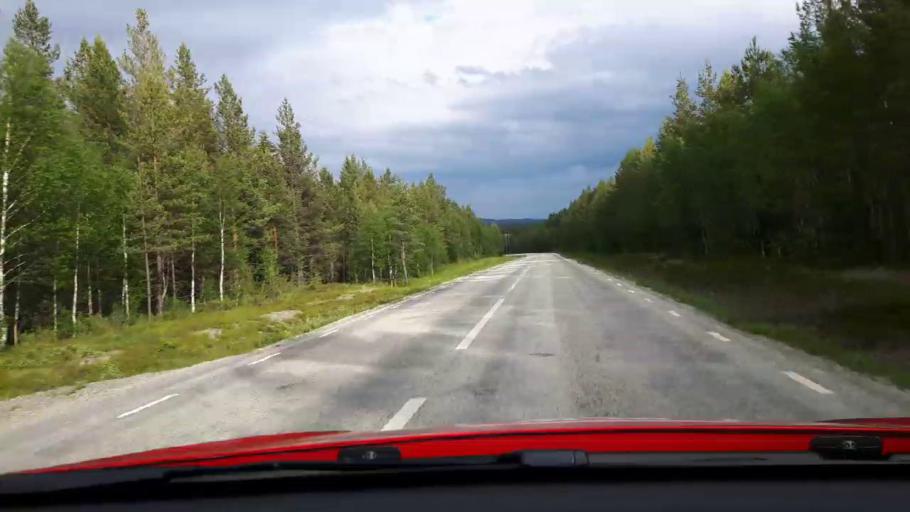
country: SE
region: Jaemtland
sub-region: Bergs Kommun
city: Hoverberg
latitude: 62.6661
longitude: 14.0404
